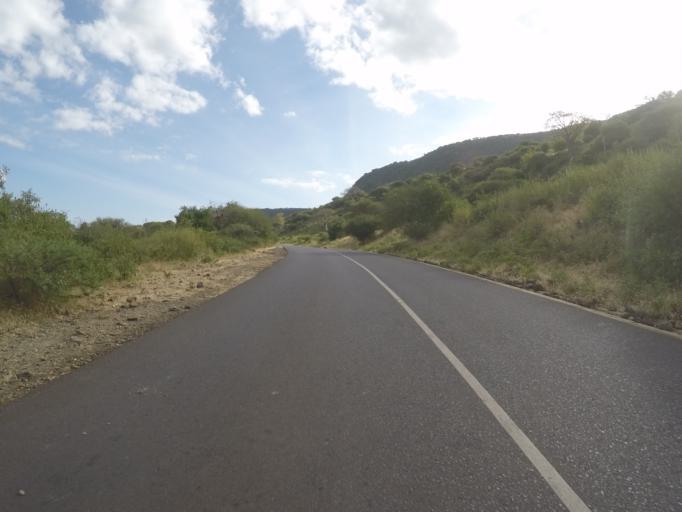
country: TZ
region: Arusha
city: Mto wa Mbu
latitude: -3.3706
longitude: 35.8414
